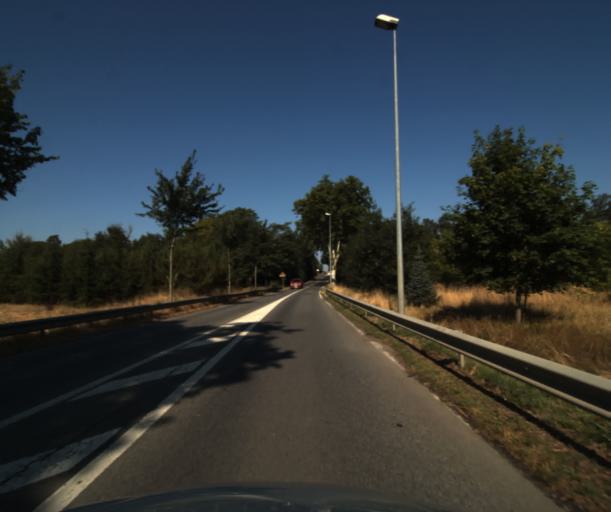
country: FR
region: Midi-Pyrenees
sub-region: Departement de la Haute-Garonne
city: Seysses
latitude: 43.4639
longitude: 1.3037
